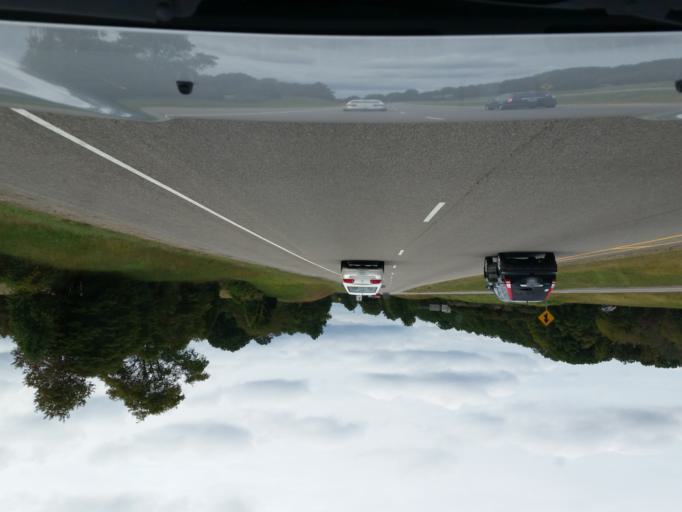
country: US
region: Virginia
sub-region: Henrico County
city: Sandston
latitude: 37.5181
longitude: -77.2614
